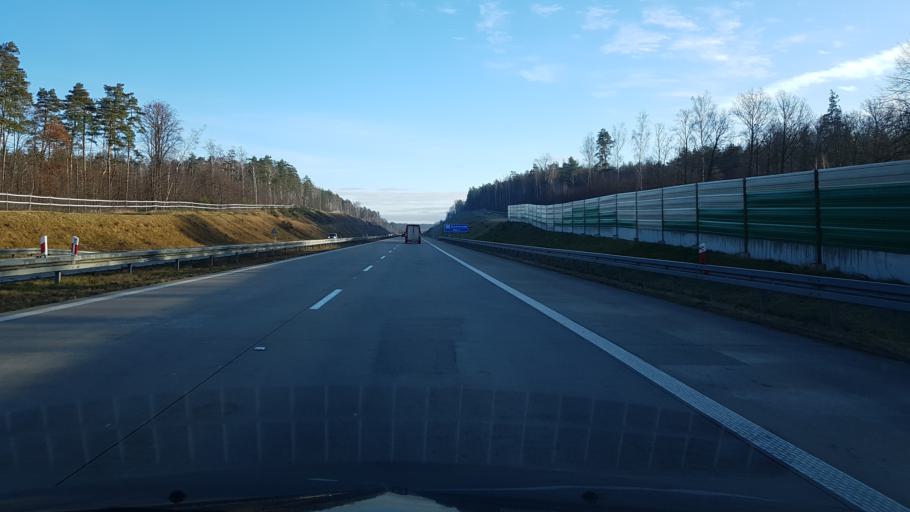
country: PL
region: Lower Silesian Voivodeship
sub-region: Powiat lubanski
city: Pisarzowice
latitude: 51.2126
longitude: 15.1927
